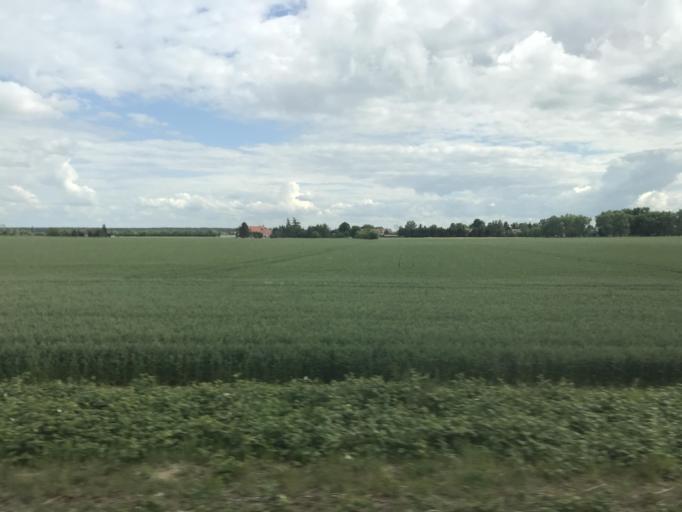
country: DE
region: Brandenburg
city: Niedergorsdorf
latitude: 51.9589
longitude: 12.9158
